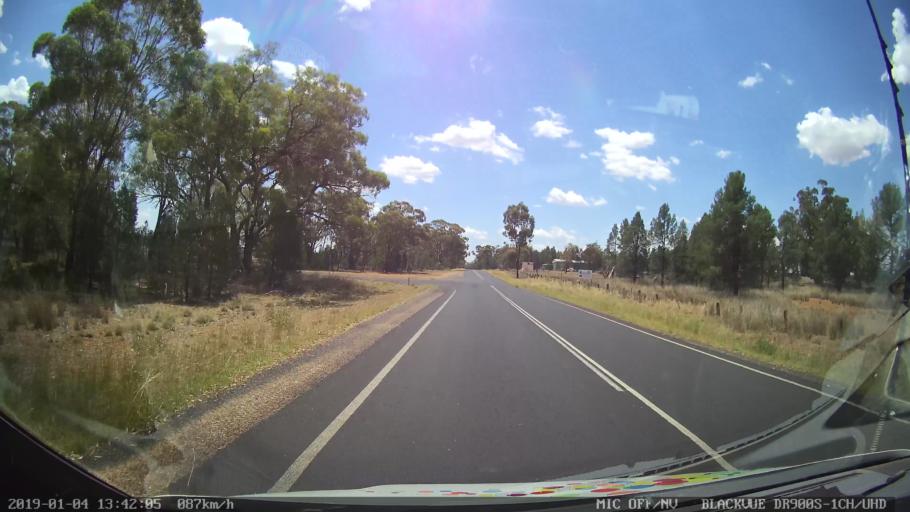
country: AU
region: New South Wales
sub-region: Dubbo Municipality
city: Dubbo
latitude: -32.4941
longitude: 148.5541
